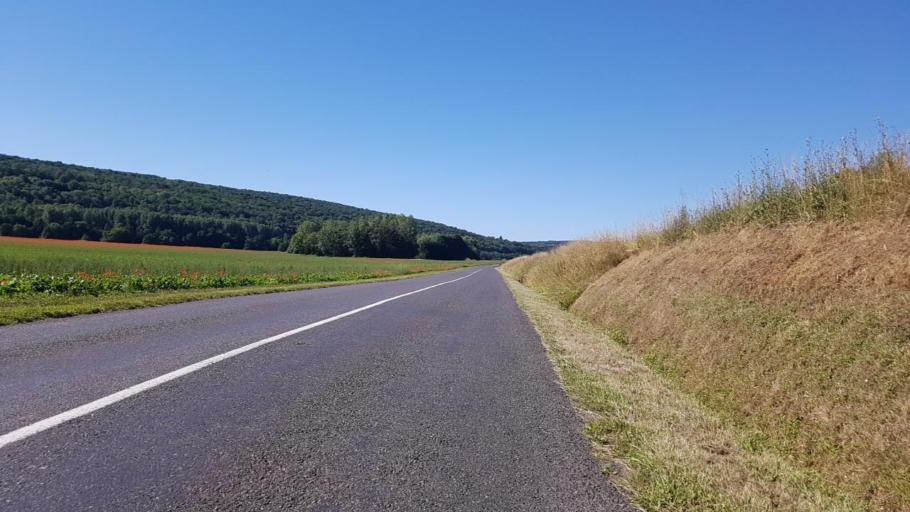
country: FR
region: Picardie
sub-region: Departement de l'Aisne
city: Chezy-sur-Marne
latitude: 48.9859
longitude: 3.3439
